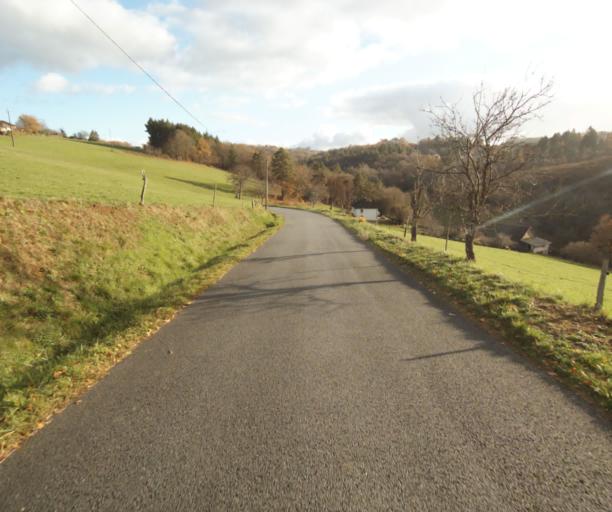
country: FR
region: Limousin
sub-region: Departement de la Correze
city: Laguenne
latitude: 45.2355
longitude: 1.7811
